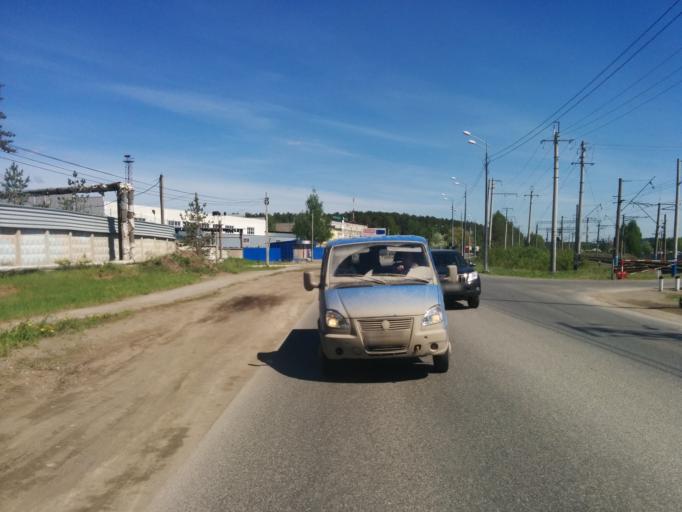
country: RU
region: Perm
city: Kondratovo
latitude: 58.0391
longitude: 56.1630
